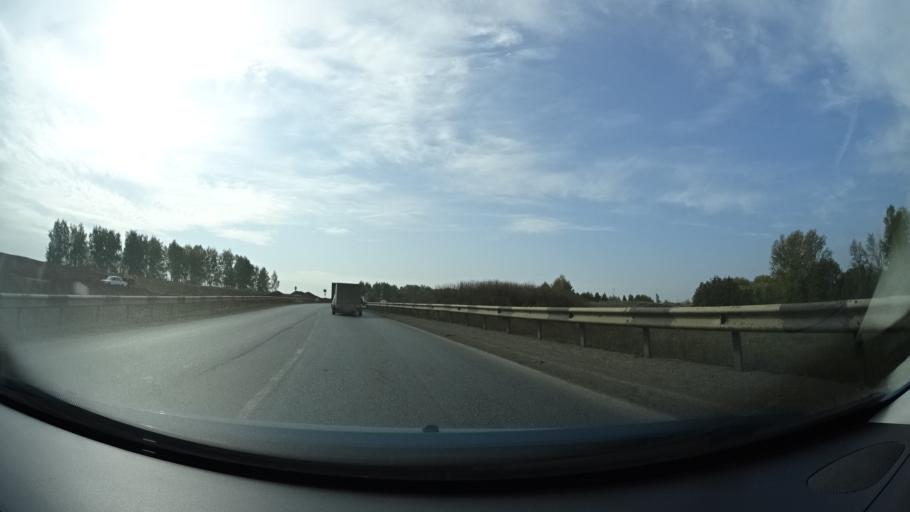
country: RU
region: Bashkortostan
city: Buzdyak
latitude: 54.6306
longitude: 54.4639
